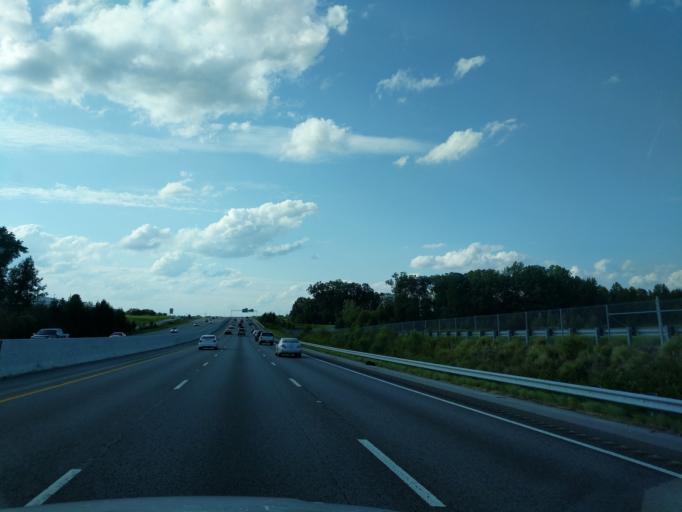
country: US
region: South Carolina
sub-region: Greenville County
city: Fountain Inn
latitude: 34.6986
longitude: -82.2330
